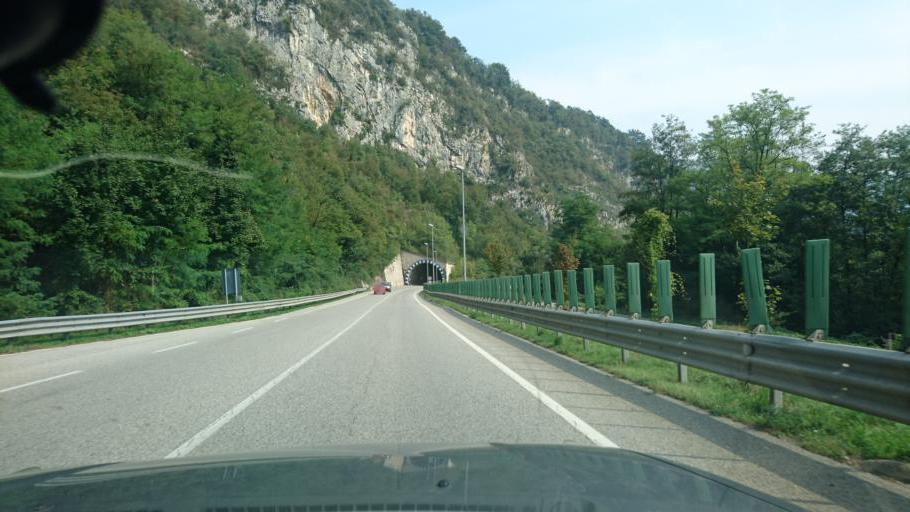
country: IT
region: Lombardy
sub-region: Provincia di Brescia
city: Sabbio Chiese
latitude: 45.6508
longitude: 10.4454
